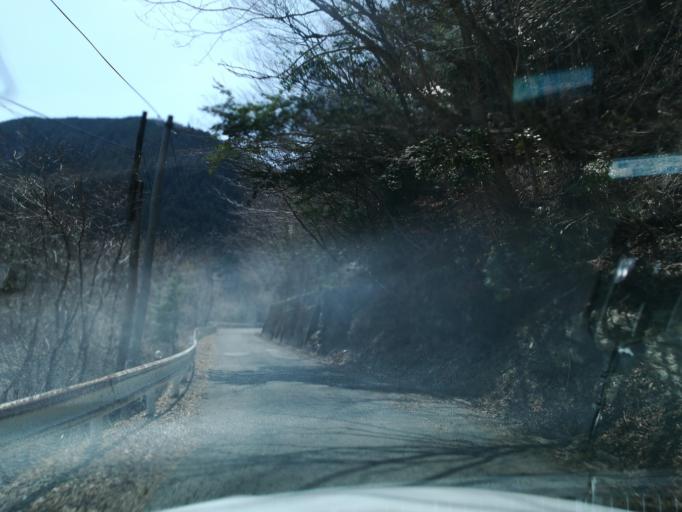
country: JP
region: Tokushima
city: Wakimachi
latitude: 33.8520
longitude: 134.0316
